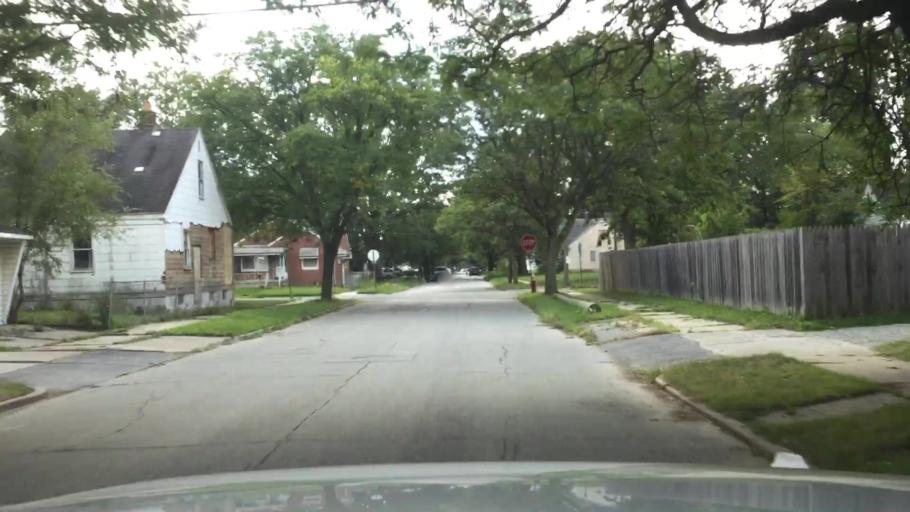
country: US
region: Michigan
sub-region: Wayne County
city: Dearborn Heights
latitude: 42.3475
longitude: -83.2233
